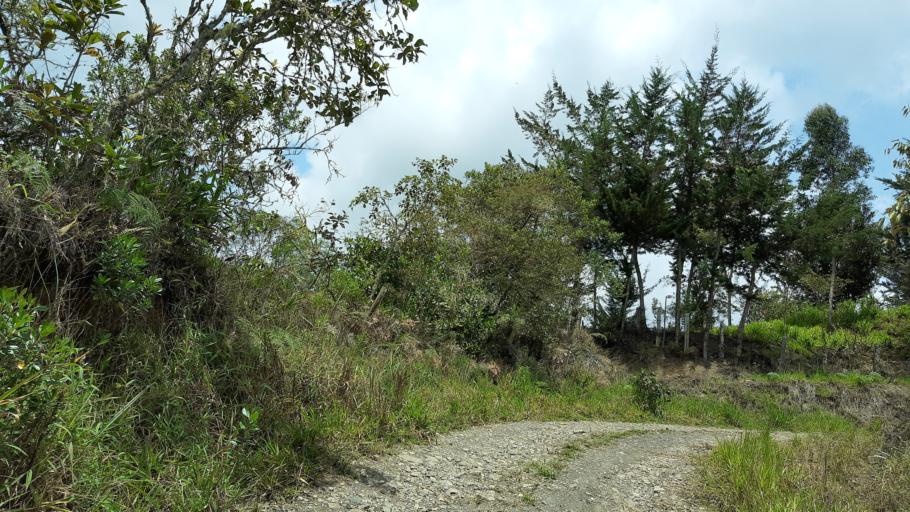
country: CO
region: Boyaca
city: Garagoa
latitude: 5.0611
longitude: -73.3563
